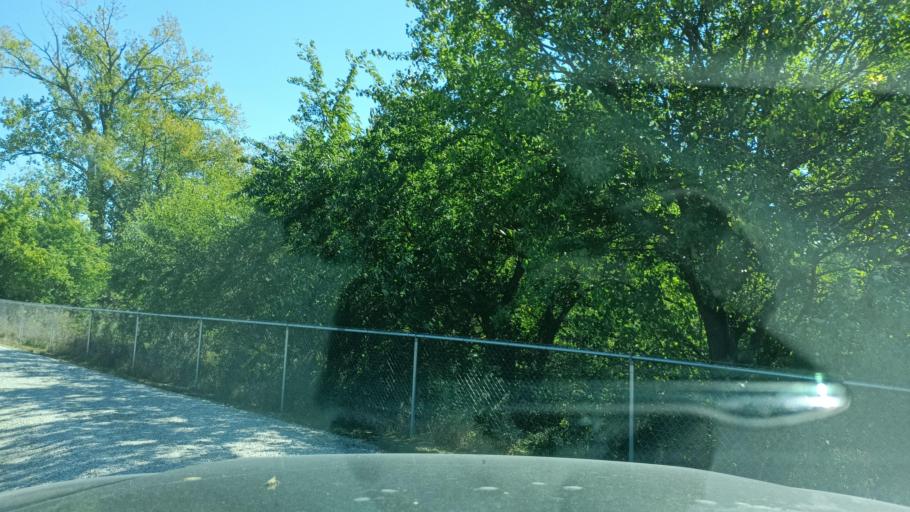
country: US
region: Illinois
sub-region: McLean County
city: Danvers
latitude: 40.5945
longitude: -89.2037
